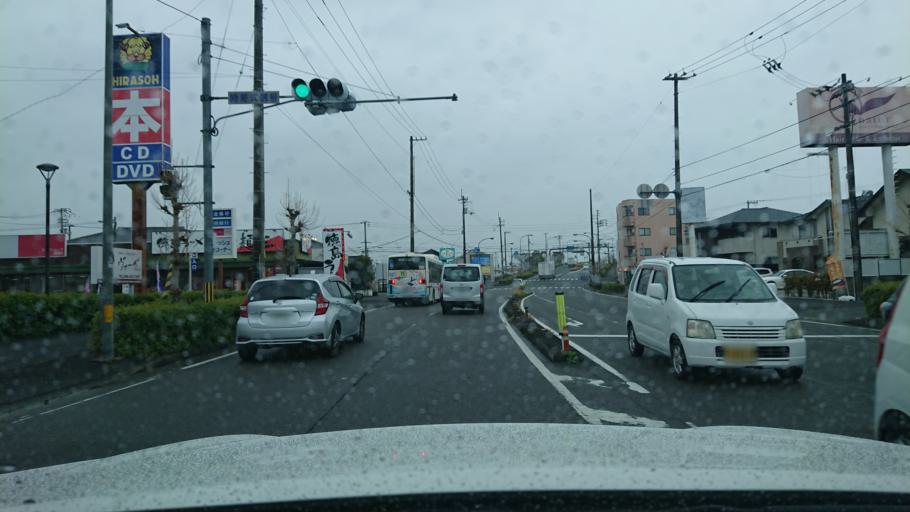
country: JP
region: Tokushima
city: Tokushima-shi
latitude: 34.0808
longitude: 134.5075
